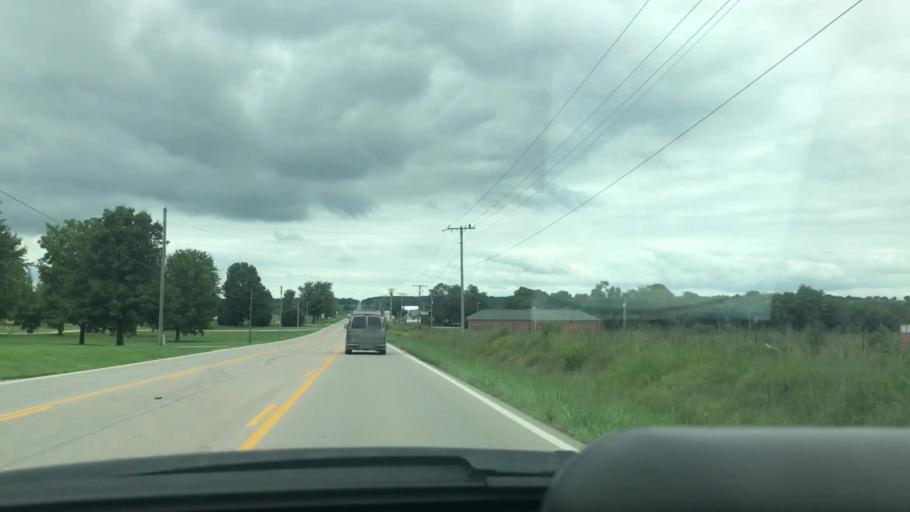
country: US
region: Missouri
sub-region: Dallas County
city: Buffalo
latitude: 37.6526
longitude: -93.1038
